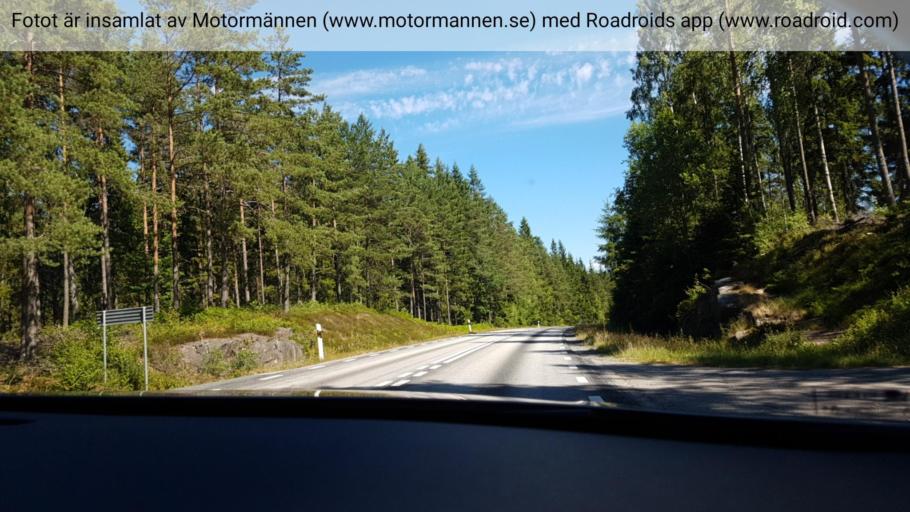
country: SE
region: Joenkoeping
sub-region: Gnosjo Kommun
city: Hillerstorp
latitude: 57.3308
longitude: 13.8183
